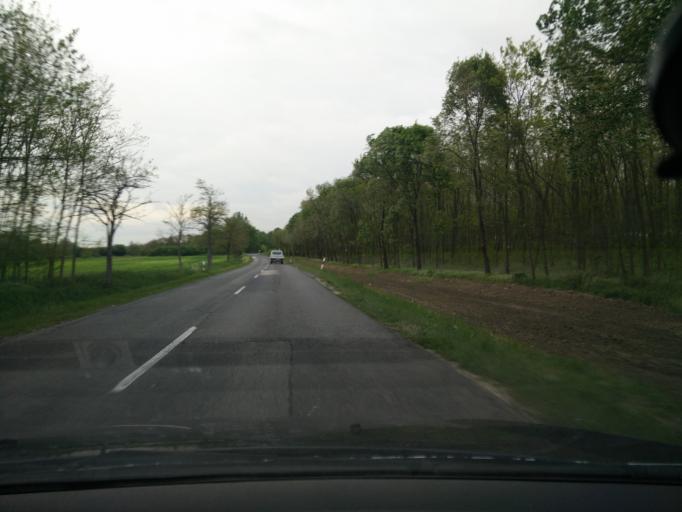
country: HU
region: Gyor-Moson-Sopron
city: Tet
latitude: 47.4834
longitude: 17.4957
